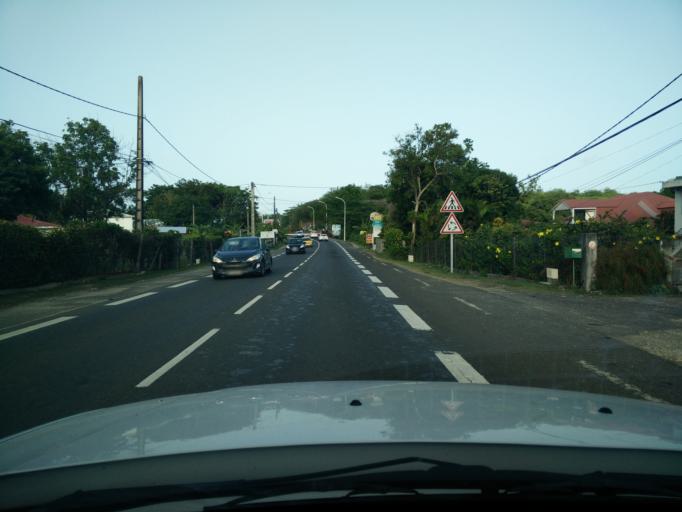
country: GP
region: Guadeloupe
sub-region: Guadeloupe
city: Le Gosier
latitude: 16.2078
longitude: -61.4625
